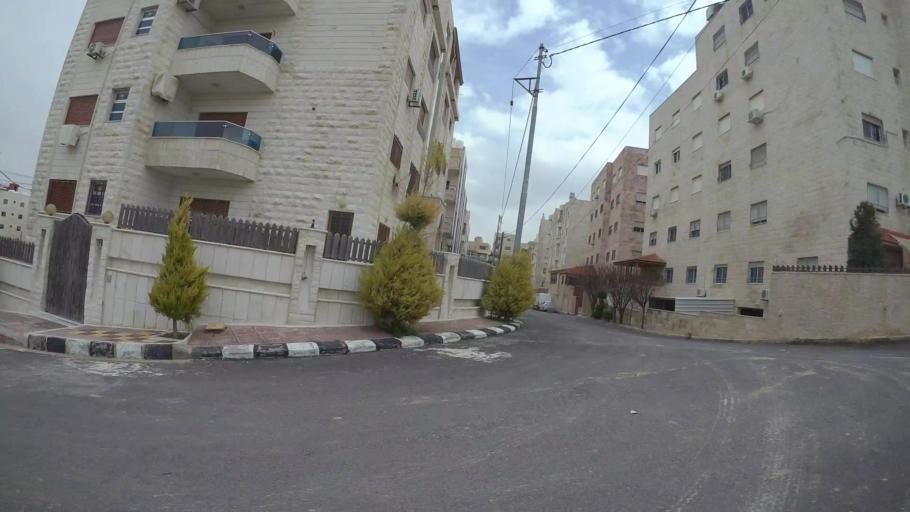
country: JO
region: Amman
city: Umm as Summaq
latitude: 31.9059
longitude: 35.8392
